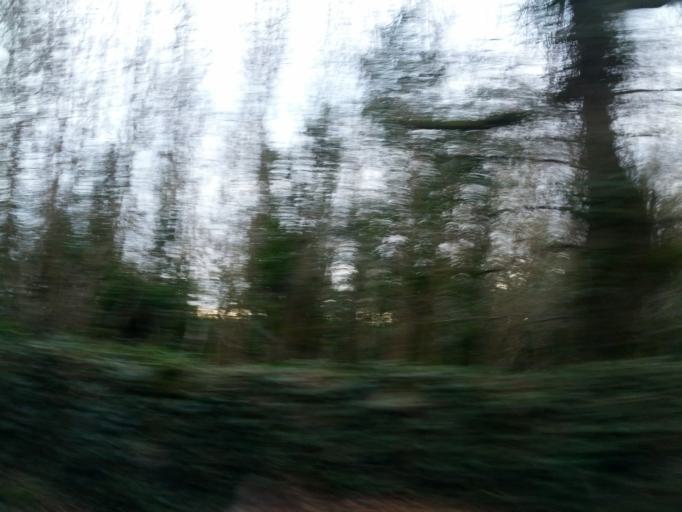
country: IE
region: Connaught
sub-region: County Galway
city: Oranmore
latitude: 53.1756
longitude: -8.8943
